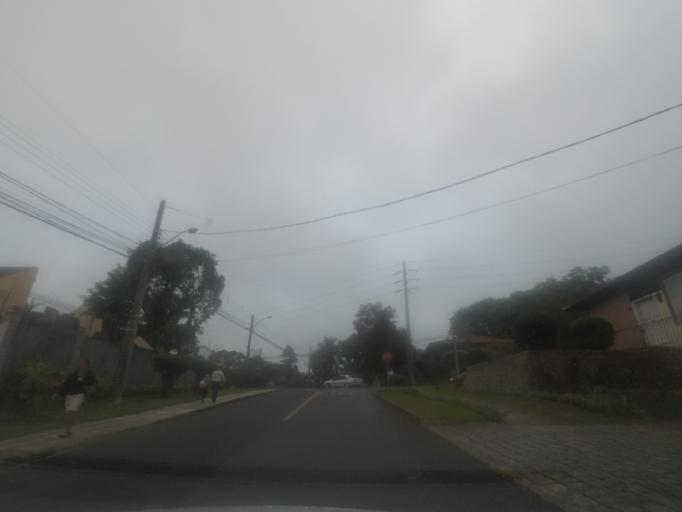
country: BR
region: Parana
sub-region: Curitiba
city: Curitiba
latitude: -25.4061
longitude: -49.2804
